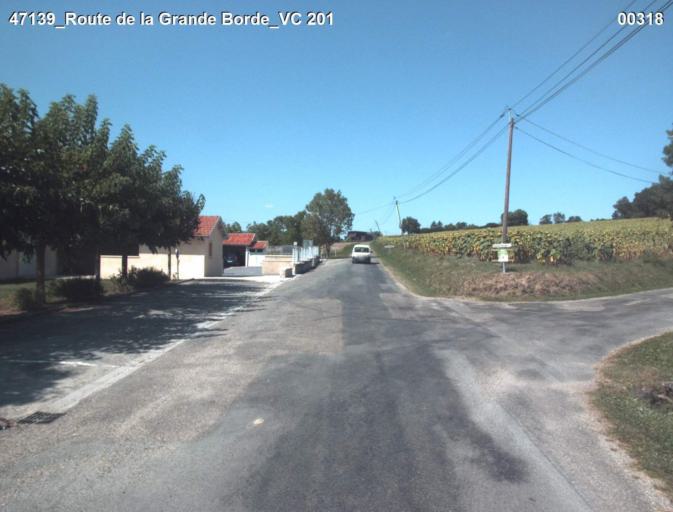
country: FR
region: Aquitaine
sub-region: Departement du Lot-et-Garonne
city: Nerac
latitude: 44.0652
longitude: 0.3931
